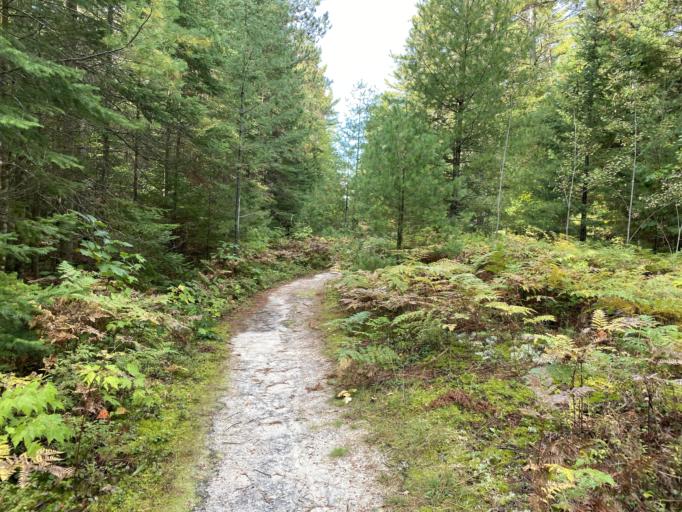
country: US
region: Michigan
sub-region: Mackinac County
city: Saint Ignace
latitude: 45.7479
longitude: -84.8884
